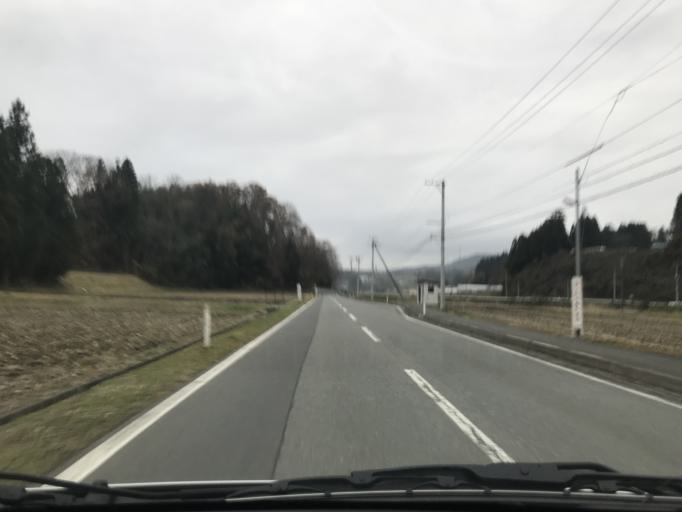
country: JP
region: Iwate
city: Mizusawa
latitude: 39.0414
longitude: 141.3543
